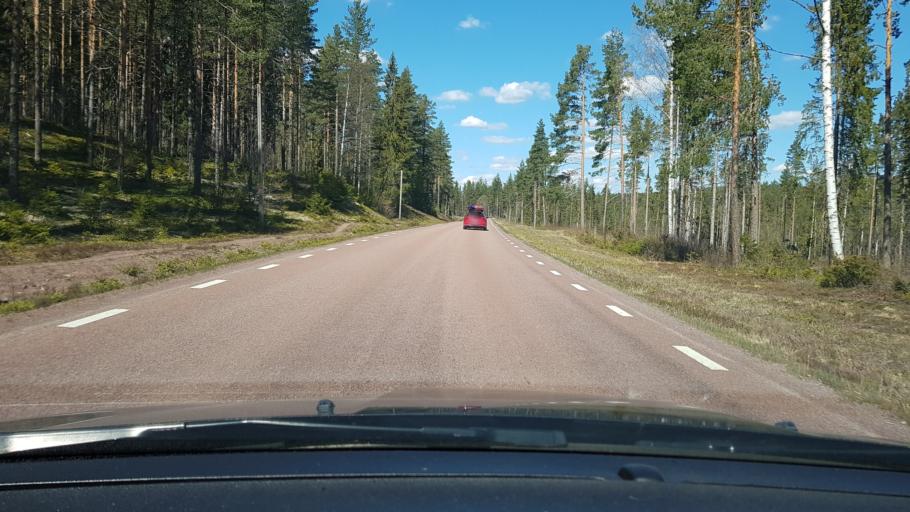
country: SE
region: Dalarna
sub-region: Alvdalens Kommun
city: AElvdalen
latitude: 61.1156
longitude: 14.0987
